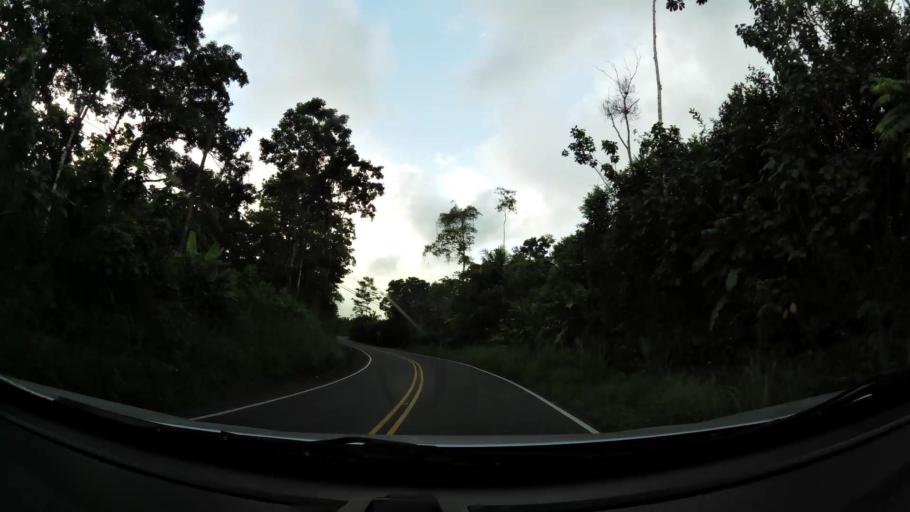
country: CR
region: Limon
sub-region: Canton de Siquirres
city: Siquirres
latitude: 9.9809
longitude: -83.5707
